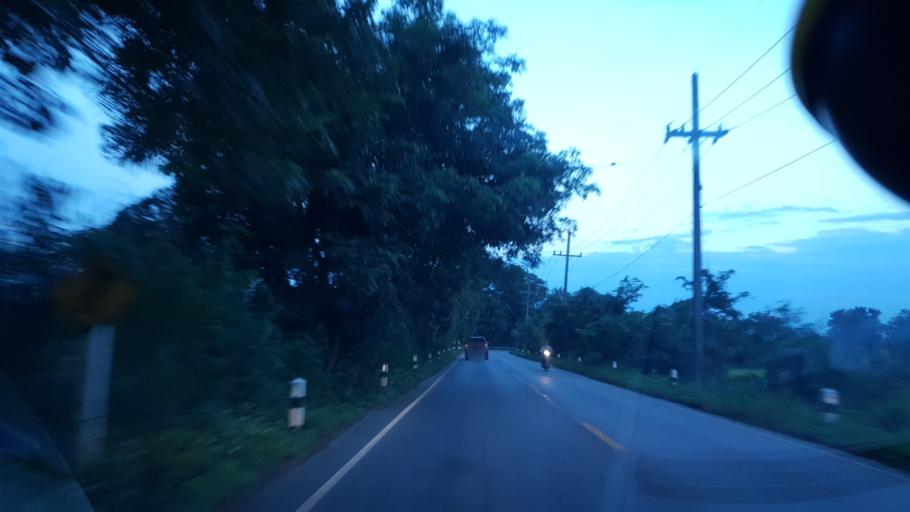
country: TH
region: Chiang Rai
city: Wiang Chiang Rung
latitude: 19.9726
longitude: 99.9779
